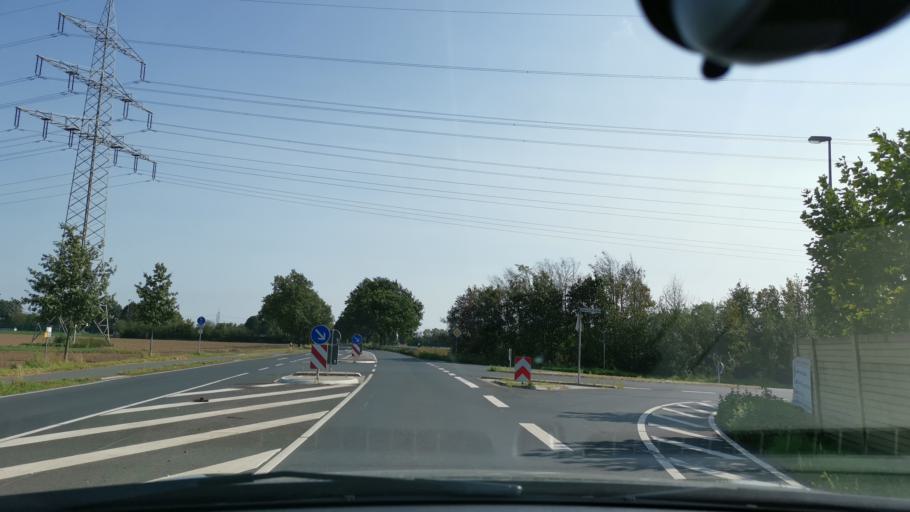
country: DE
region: North Rhine-Westphalia
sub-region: Regierungsbezirk Dusseldorf
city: Grevenbroich
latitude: 51.0818
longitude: 6.6296
